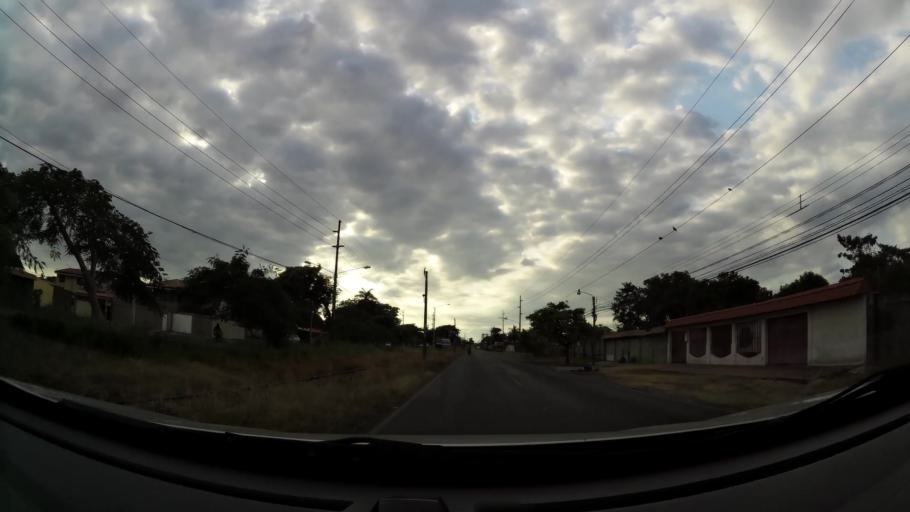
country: CR
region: Puntarenas
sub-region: Canton Central de Puntarenas
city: Chacarita
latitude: 9.9782
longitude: -84.7540
